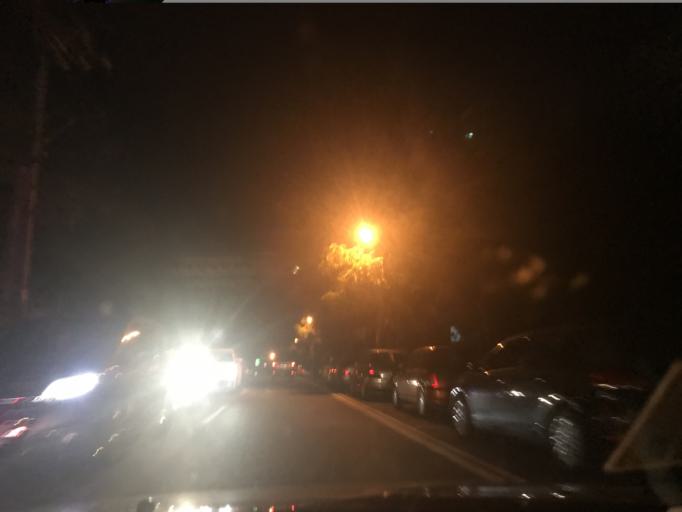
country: TW
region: Taiwan
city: Daxi
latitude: 24.9397
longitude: 121.2186
